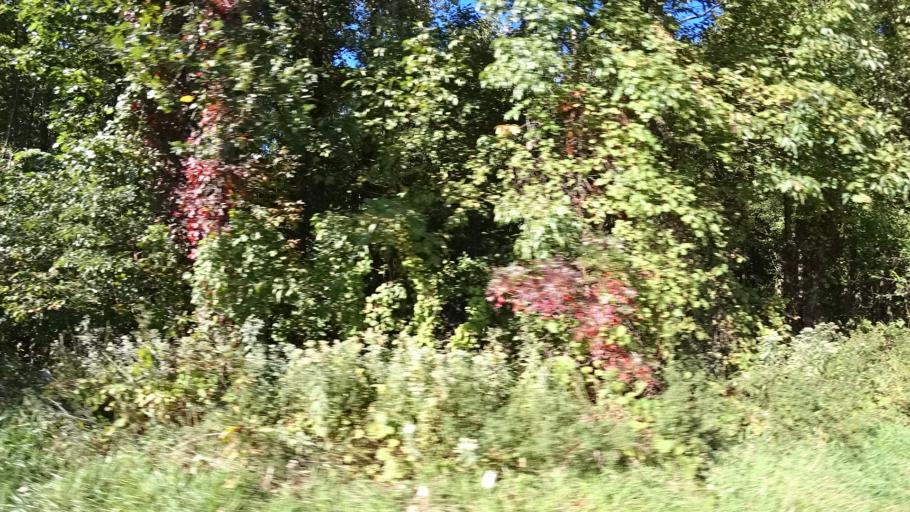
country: US
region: Indiana
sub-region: LaPorte County
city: Michigan City
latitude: 41.6825
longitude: -86.9133
